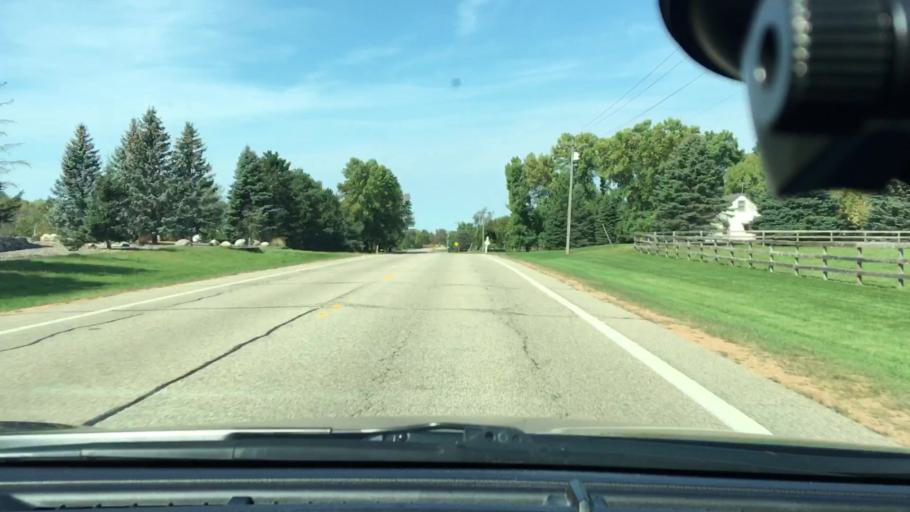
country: US
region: Minnesota
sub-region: Hennepin County
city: Corcoran
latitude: 45.1026
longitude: -93.5588
